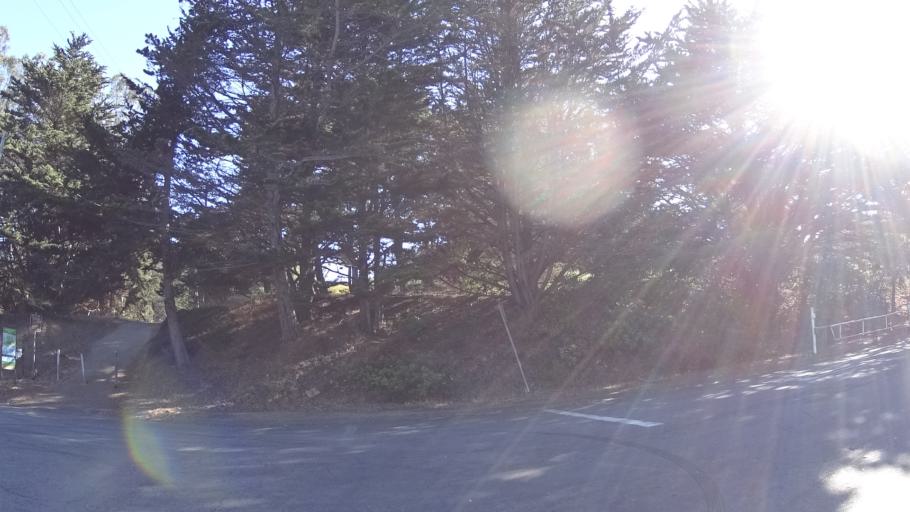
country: US
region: California
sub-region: San Mateo County
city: Brisbane
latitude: 37.7219
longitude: -122.4166
